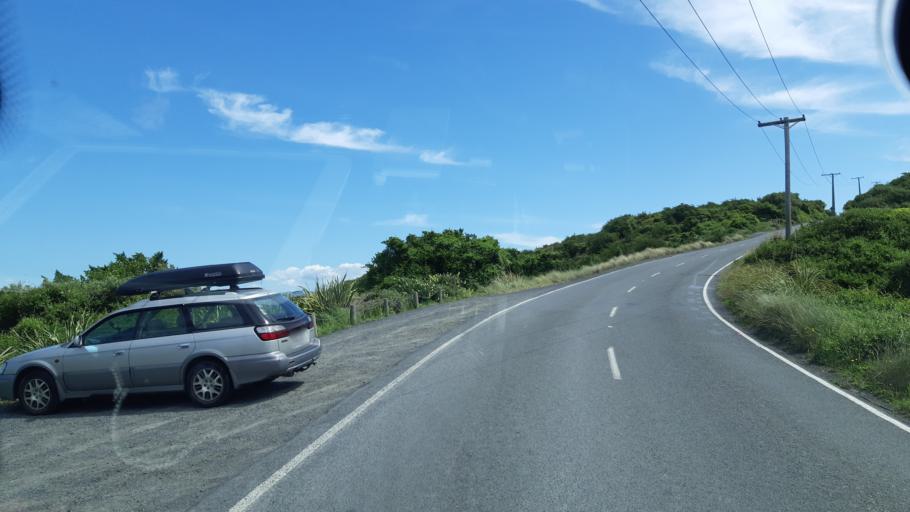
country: NZ
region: Otago
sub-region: Dunedin City
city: Dunedin
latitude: -45.9274
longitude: 170.4274
